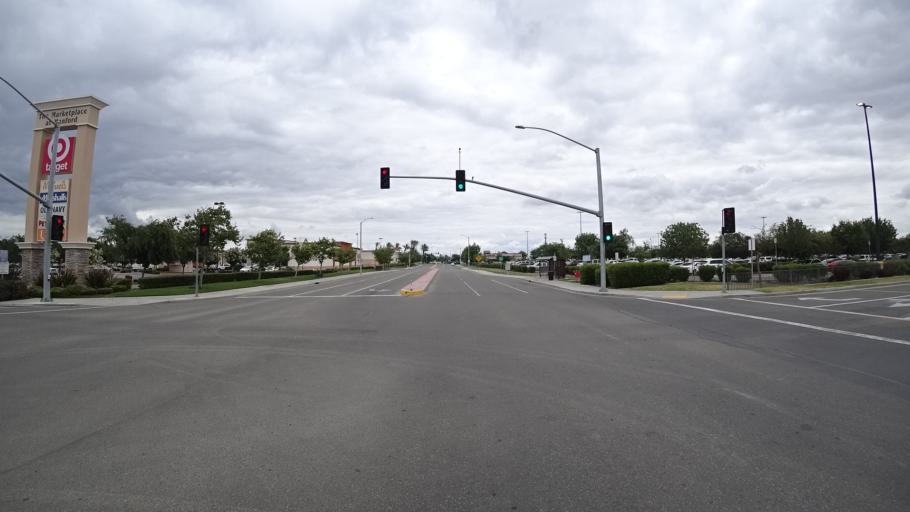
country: US
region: California
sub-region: Kings County
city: Hanford
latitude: 36.3228
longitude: -119.6758
